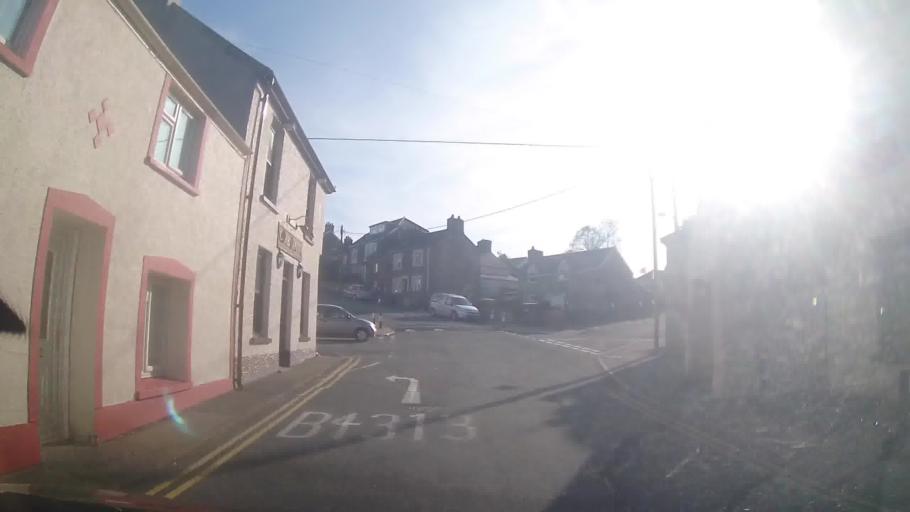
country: GB
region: Wales
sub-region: Pembrokeshire
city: Fishguard
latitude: 51.9937
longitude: -4.9748
